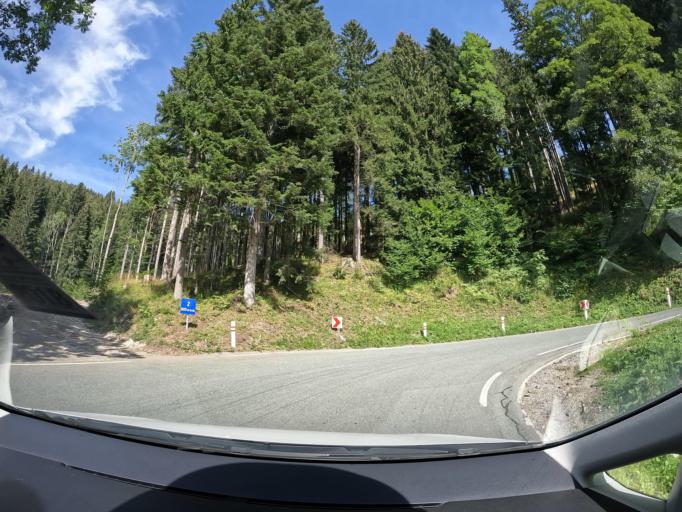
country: AT
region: Carinthia
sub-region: Politischer Bezirk Feldkirchen
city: Glanegg
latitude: 46.7432
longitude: 14.2180
